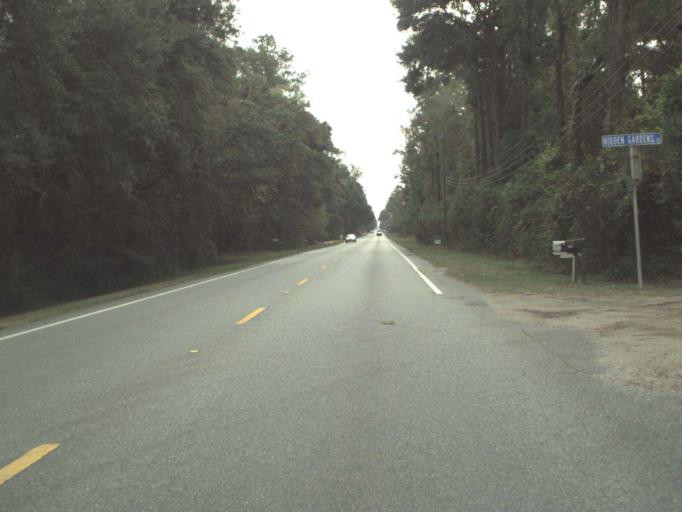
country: US
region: Florida
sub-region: Leon County
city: Woodville
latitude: 30.2895
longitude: -84.2423
